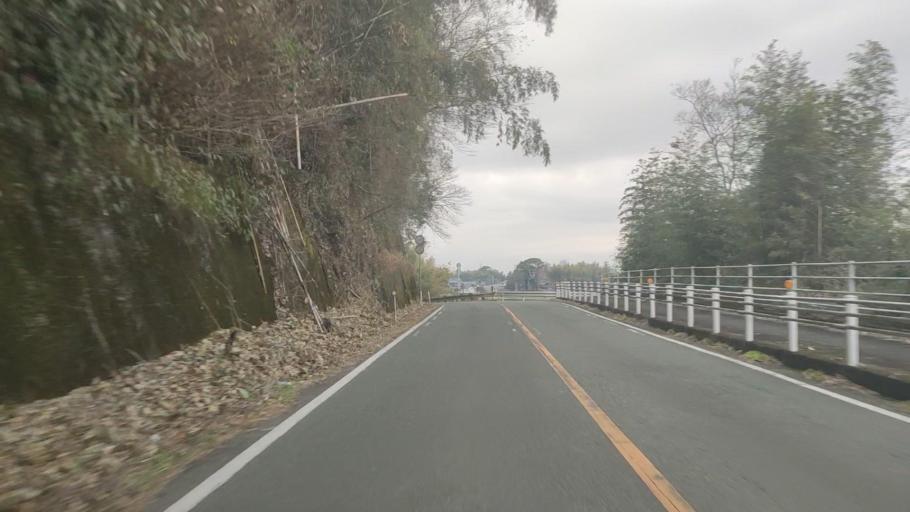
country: JP
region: Kumamoto
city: Ozu
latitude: 32.8526
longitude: 130.8663
